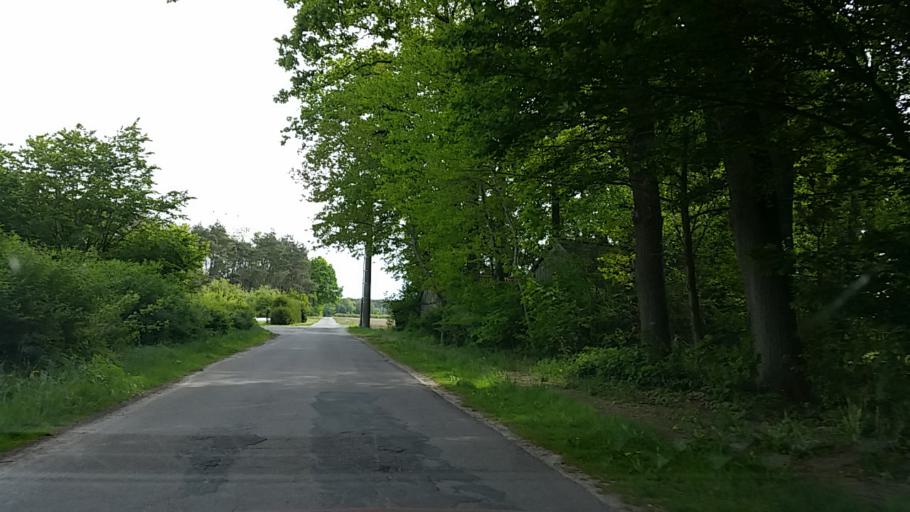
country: DE
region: Lower Saxony
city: Luder
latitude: 52.7672
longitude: 10.6920
